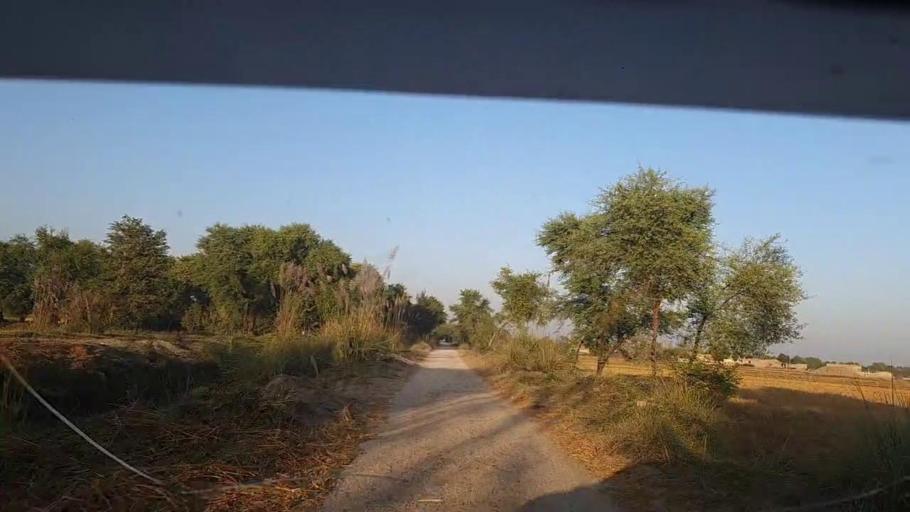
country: PK
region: Sindh
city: Ratodero
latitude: 27.8753
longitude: 68.1987
